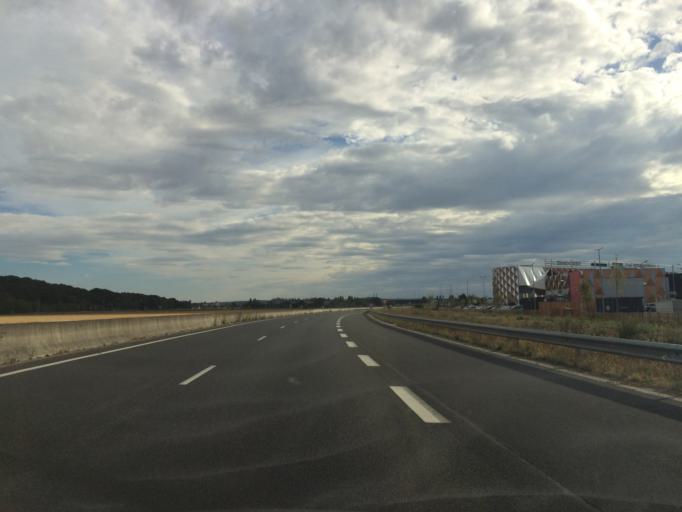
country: FR
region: Ile-de-France
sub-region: Departement de l'Essonne
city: Marolles-en-Hurepoix
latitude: 48.5812
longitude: 2.3040
